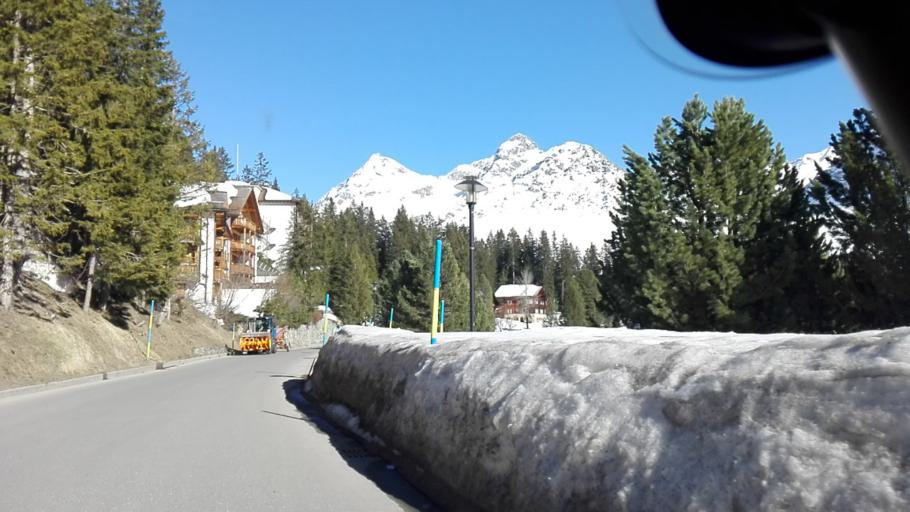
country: CH
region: Grisons
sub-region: Plessur District
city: Arosa
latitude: 46.7866
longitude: 9.6809
